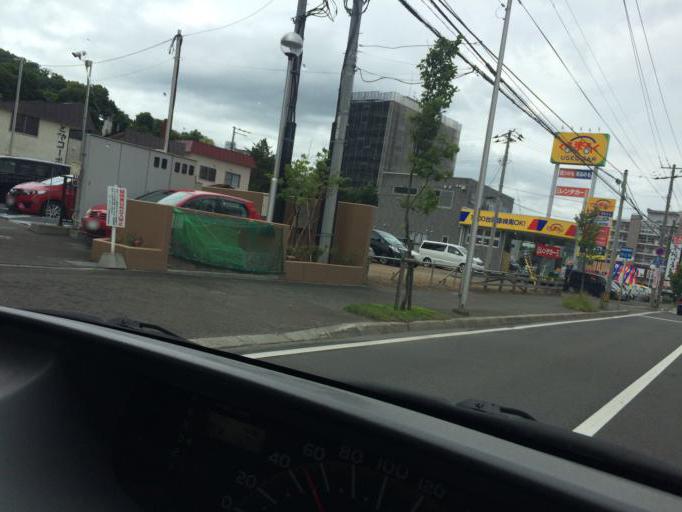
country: JP
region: Hokkaido
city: Sapporo
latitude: 43.0361
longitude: 141.3322
